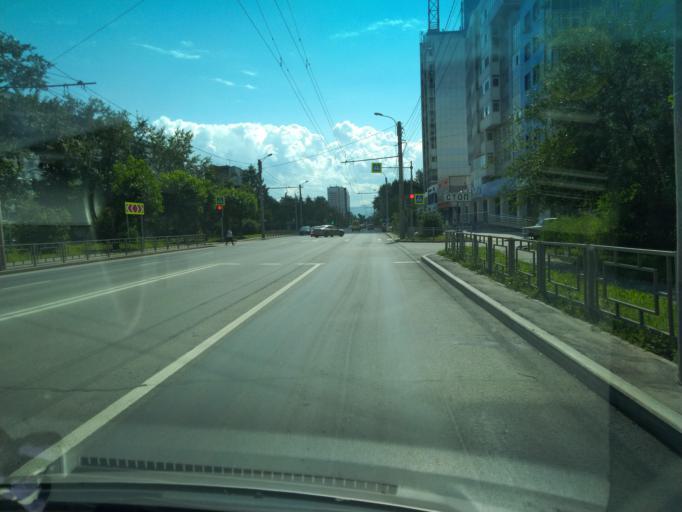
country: RU
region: Krasnoyarskiy
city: Solnechnyy
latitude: 56.0476
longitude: 92.9415
